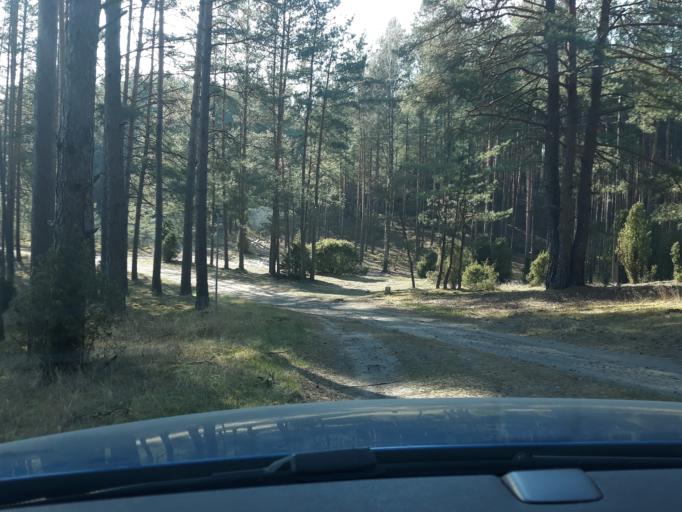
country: PL
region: Pomeranian Voivodeship
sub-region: Powiat bytowski
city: Lipnica
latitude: 53.8975
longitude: 17.4145
